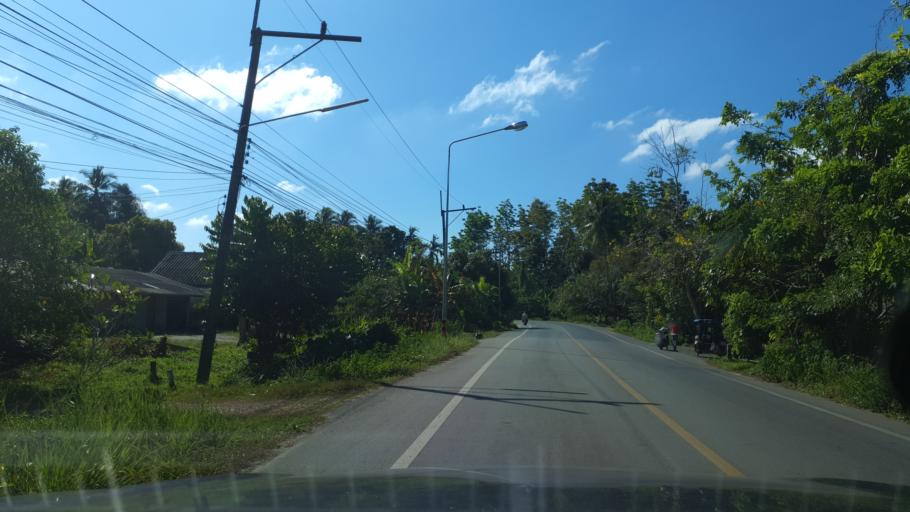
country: TH
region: Phangnga
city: Ban Ao Nang
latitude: 8.0668
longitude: 98.8093
